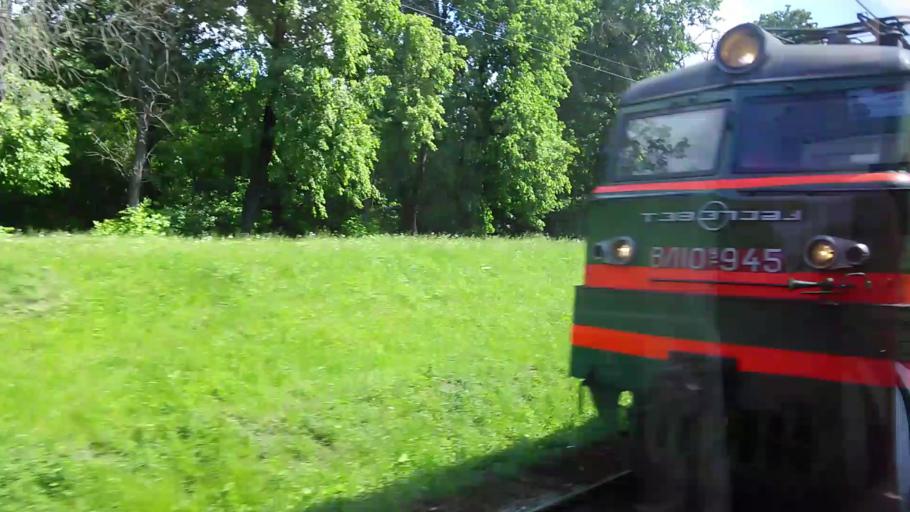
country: RU
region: Moscow
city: Novovladykino
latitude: 55.8132
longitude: 37.5790
